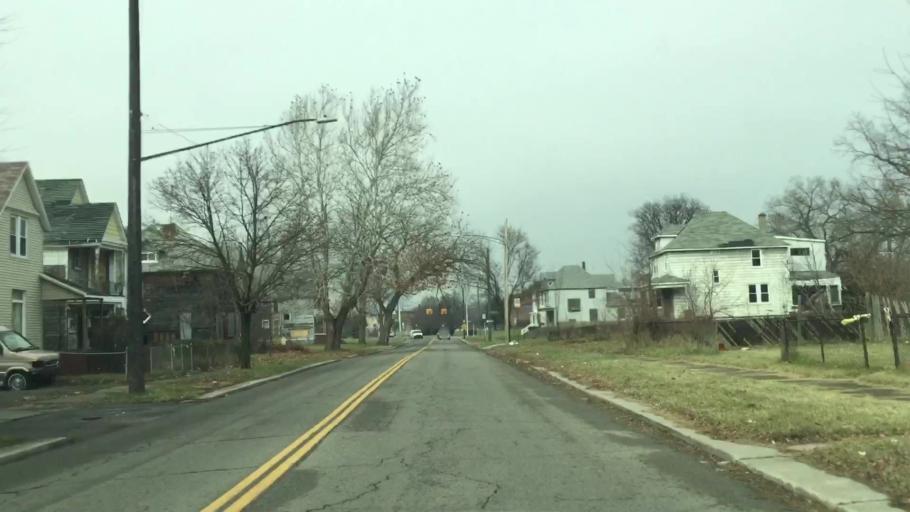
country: US
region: Michigan
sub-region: Wayne County
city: Highland Park
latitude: 42.3545
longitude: -83.0952
